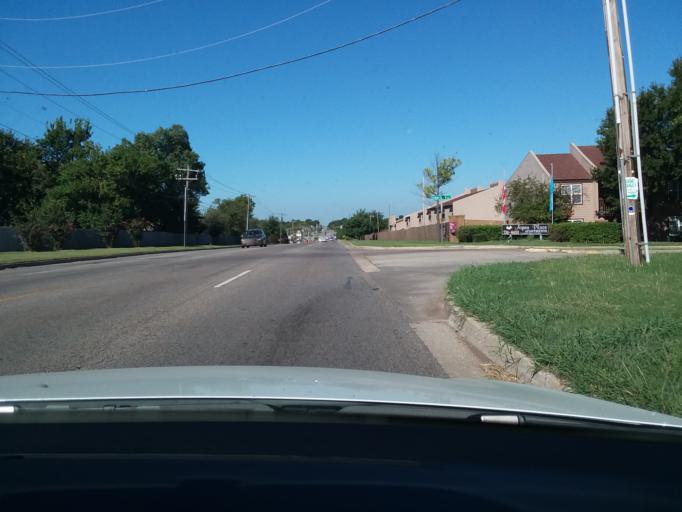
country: US
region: Oklahoma
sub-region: Oklahoma County
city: The Village
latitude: 35.5947
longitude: -97.5614
